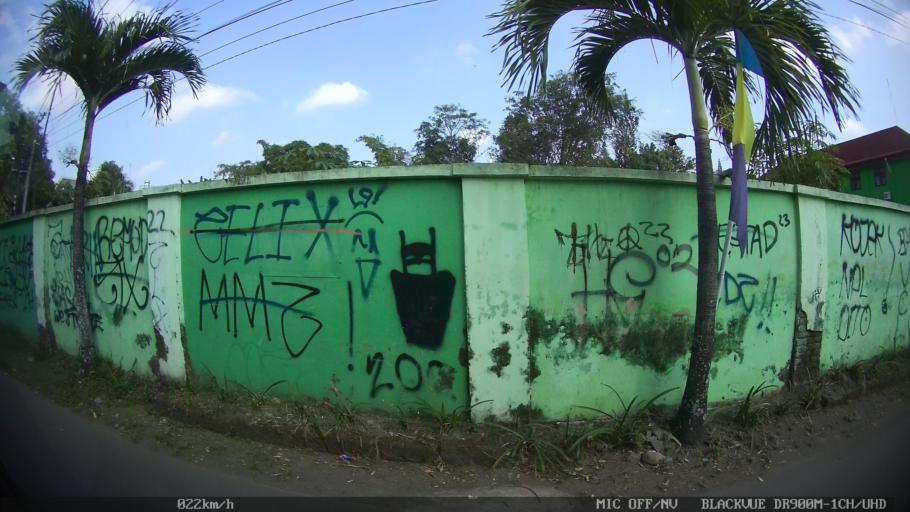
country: ID
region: Daerah Istimewa Yogyakarta
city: Yogyakarta
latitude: -7.7773
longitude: 110.3910
